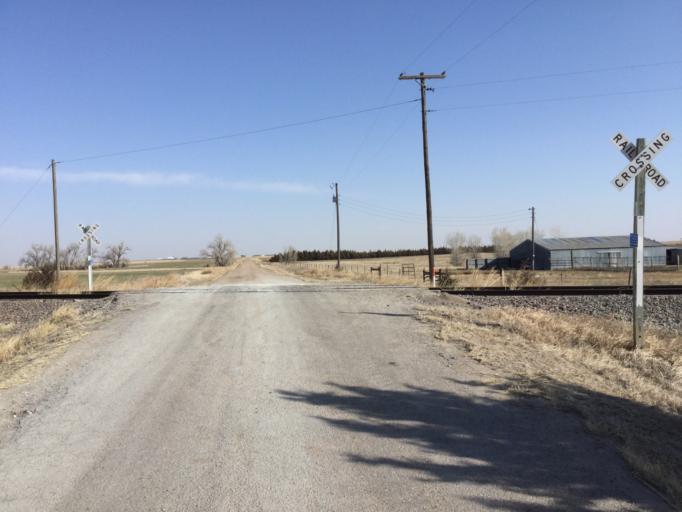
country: US
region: Kansas
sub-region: Rush County
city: La Crosse
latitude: 38.5395
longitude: -99.3283
